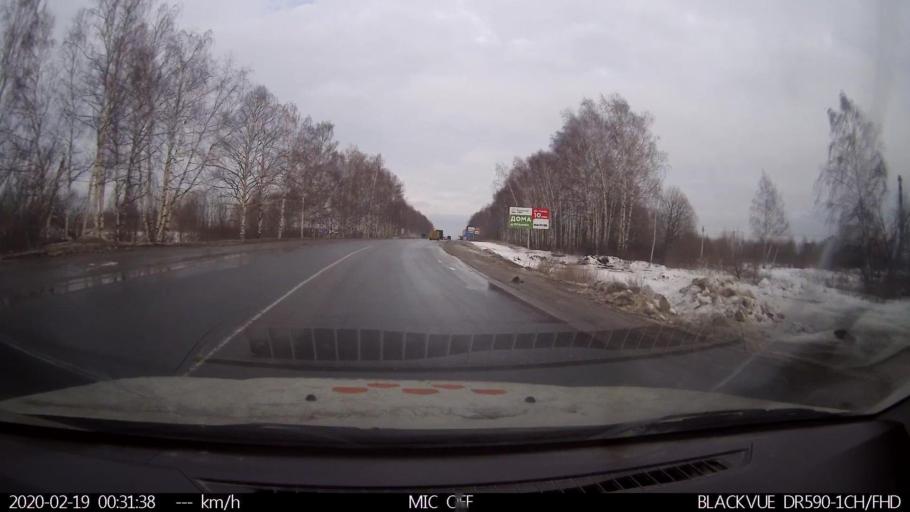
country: RU
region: Nizjnij Novgorod
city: Afonino
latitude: 56.2205
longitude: 44.0573
